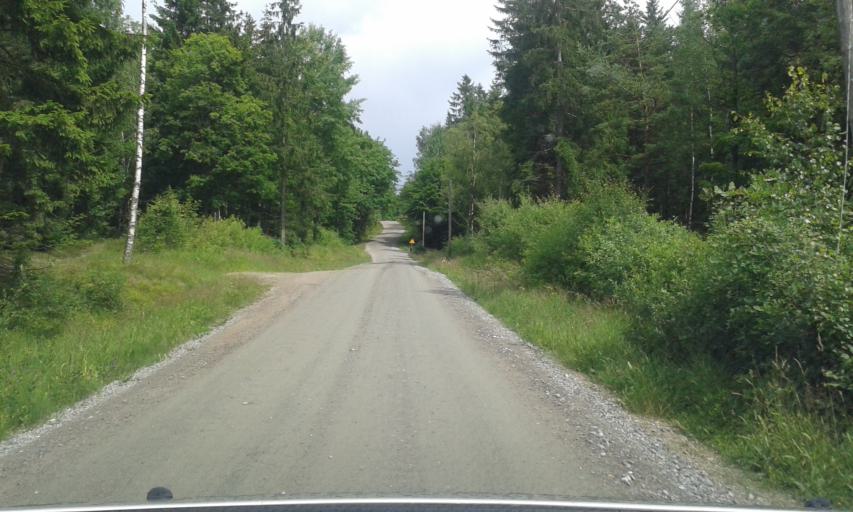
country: SE
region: Vaestra Goetaland
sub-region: Kungalvs Kommun
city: Diserod
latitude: 57.9649
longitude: 12.0188
